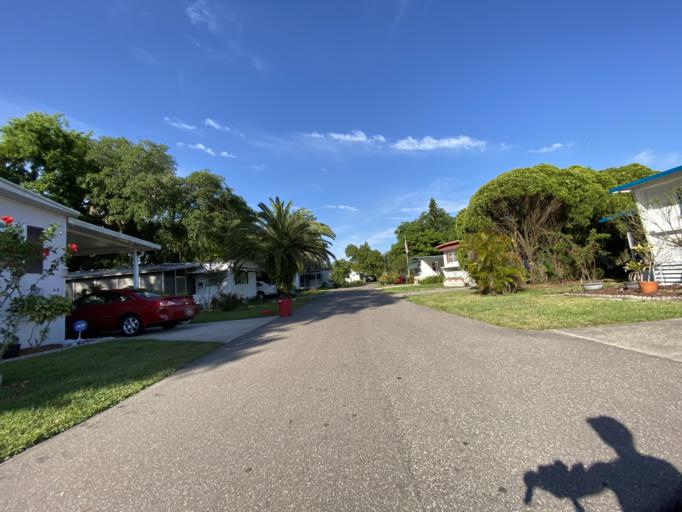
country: US
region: Florida
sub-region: Volusia County
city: South Daytona
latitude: 29.1745
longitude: -81.0192
